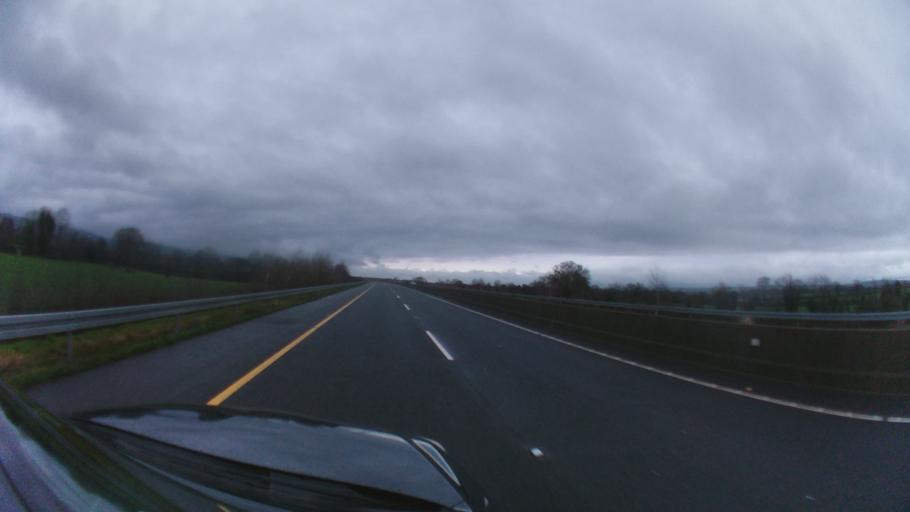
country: IE
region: Leinster
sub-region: County Carlow
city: Bagenalstown
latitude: 52.7308
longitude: -7.0023
